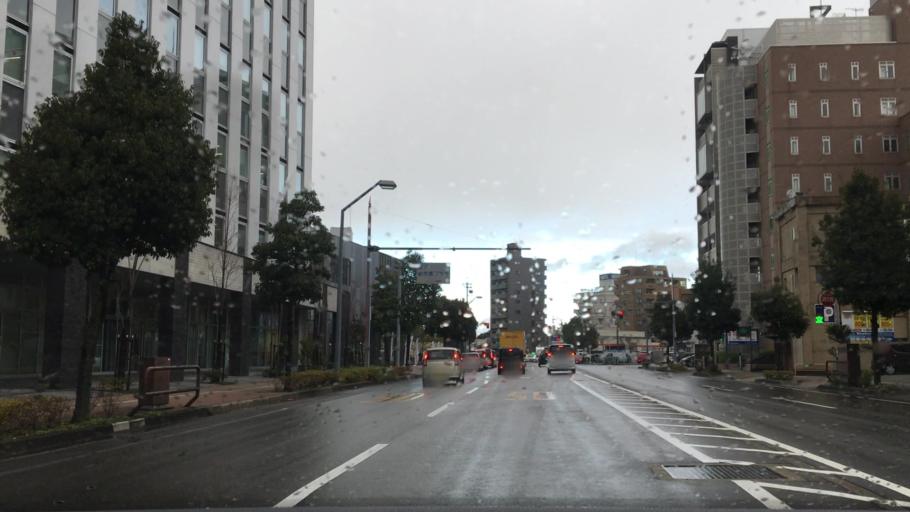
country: JP
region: Ishikawa
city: Kanazawa-shi
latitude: 36.5810
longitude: 136.6467
